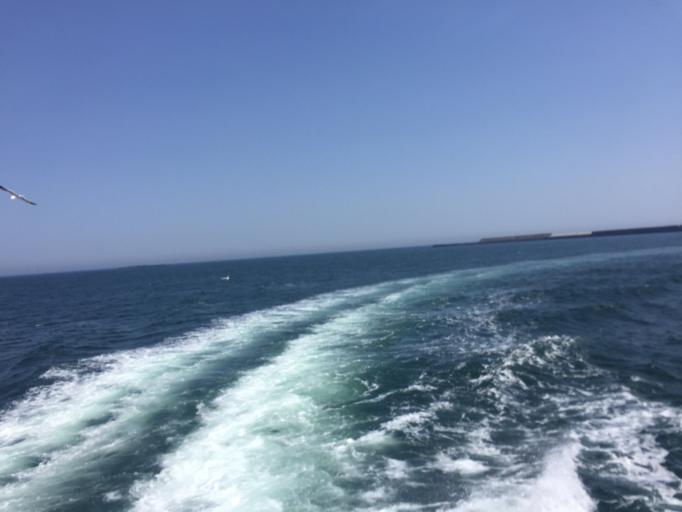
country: JP
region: Fukushima
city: Iwaki
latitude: 36.9185
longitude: 140.8967
